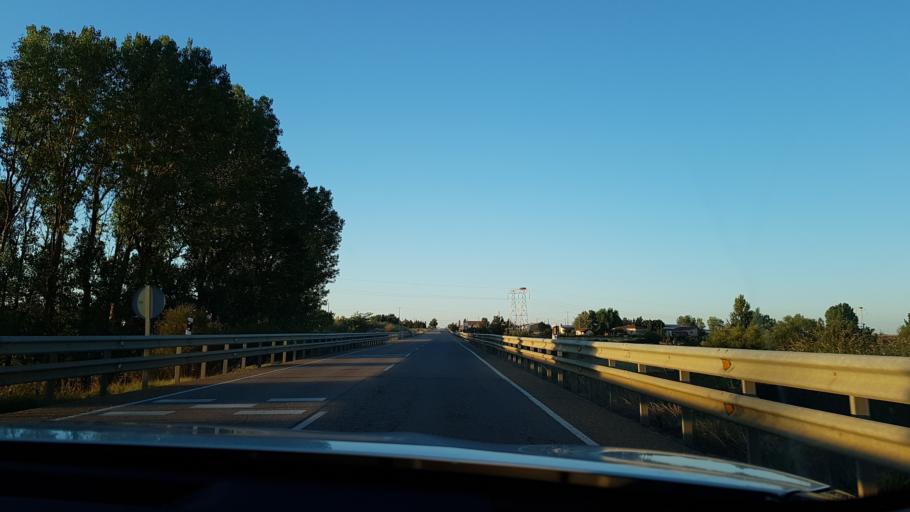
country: ES
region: Castille and Leon
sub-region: Provincia de Zamora
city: Montamarta
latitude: 41.6437
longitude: -5.8014
